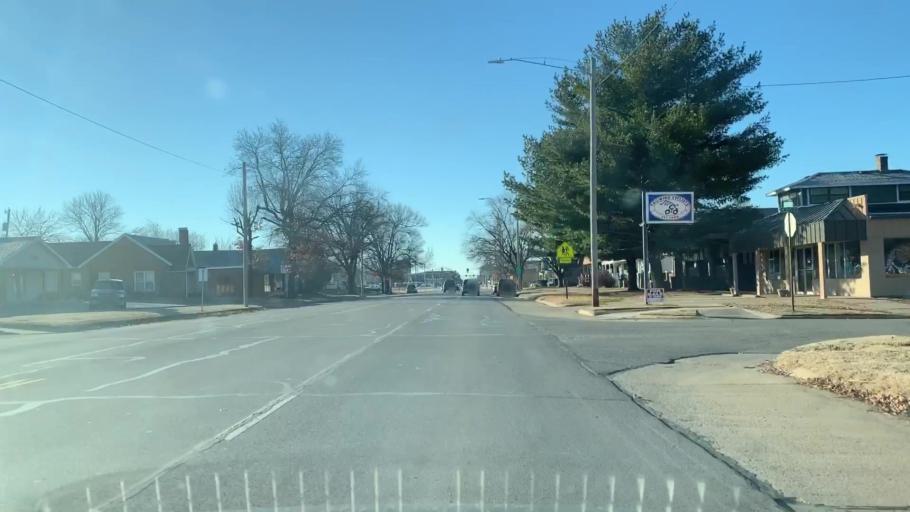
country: US
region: Kansas
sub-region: Crawford County
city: Pittsburg
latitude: 37.4222
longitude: -94.7050
